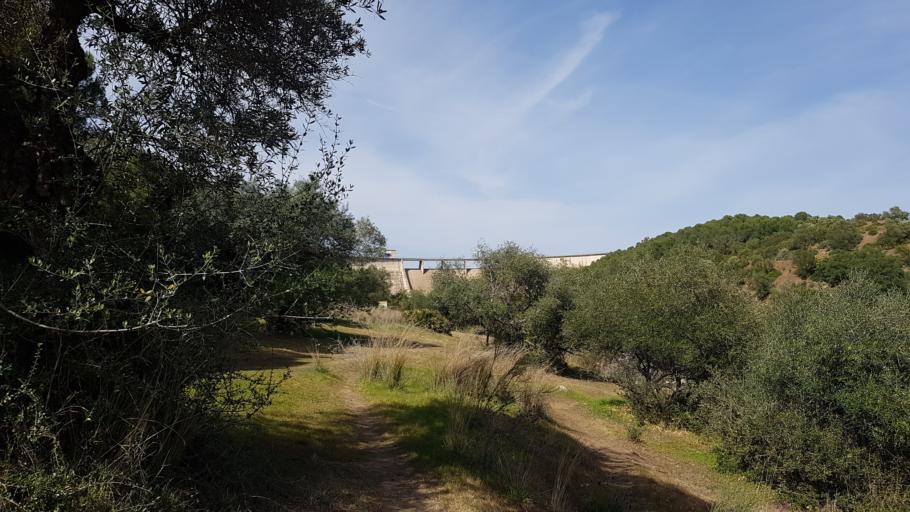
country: ES
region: Andalusia
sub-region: Provincia de Sevilla
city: Guillena
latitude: 37.5631
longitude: -6.0500
